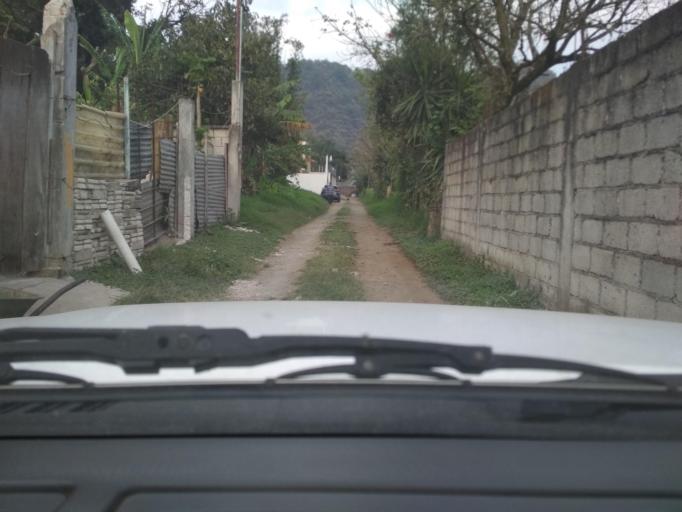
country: MX
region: Veracruz
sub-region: Mariano Escobedo
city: Palmira
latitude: 18.8721
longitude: -97.1026
